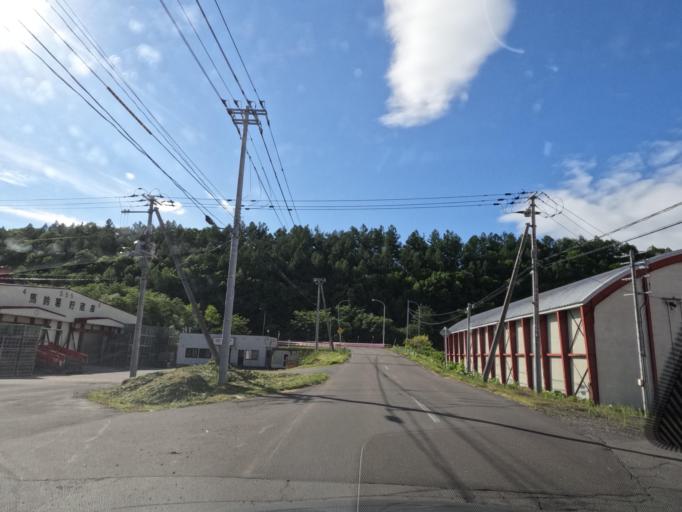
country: JP
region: Hokkaido
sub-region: Asahikawa-shi
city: Asahikawa
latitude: 43.5913
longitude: 142.4521
